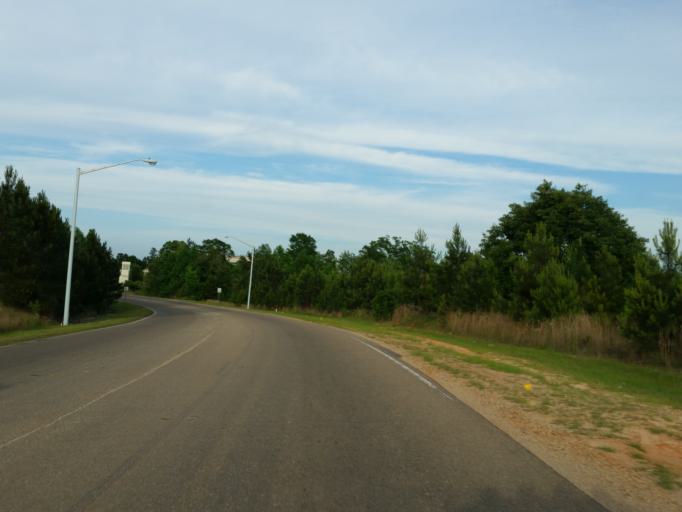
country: US
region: Mississippi
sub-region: Lamar County
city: West Hattiesburg
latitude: 31.3013
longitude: -89.3631
